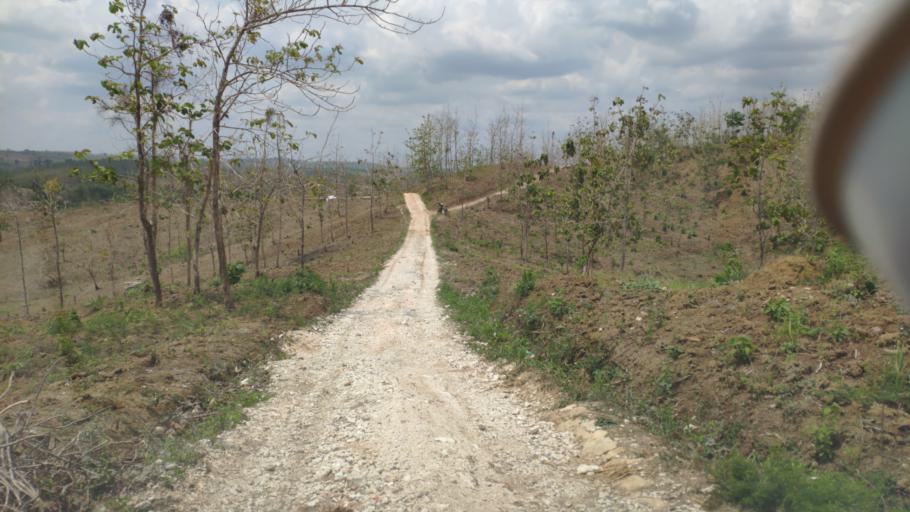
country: ID
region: Central Java
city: Klopoduwur
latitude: -7.0511
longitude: 111.4021
